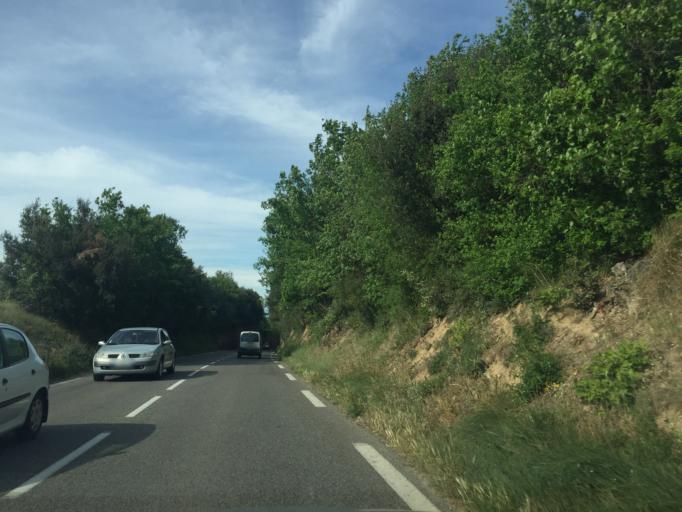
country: FR
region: Provence-Alpes-Cote d'Azur
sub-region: Departement des Alpes-de-Haute-Provence
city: Sainte-Tulle
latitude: 43.7764
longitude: 5.8168
